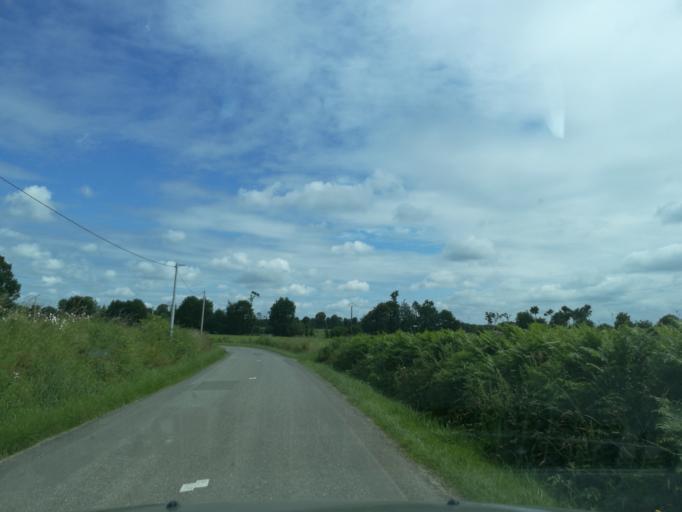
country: FR
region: Brittany
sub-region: Departement d'Ille-et-Vilaine
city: Bedee
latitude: 48.1921
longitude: -1.9881
